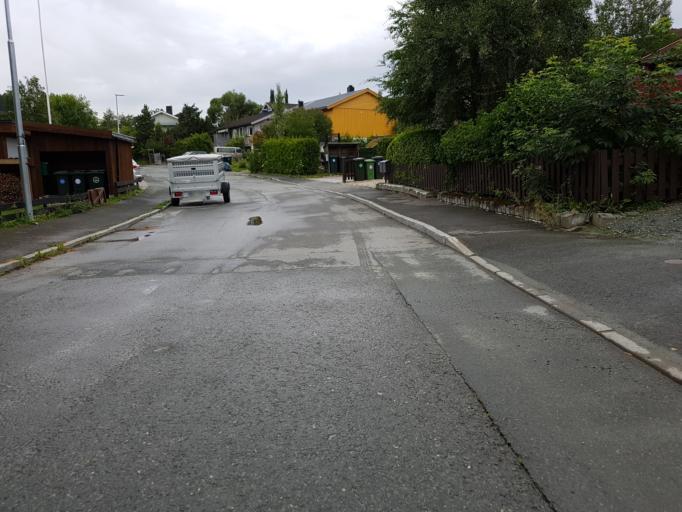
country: NO
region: Sor-Trondelag
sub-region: Trondheim
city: Trondheim
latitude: 63.3867
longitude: 10.3580
